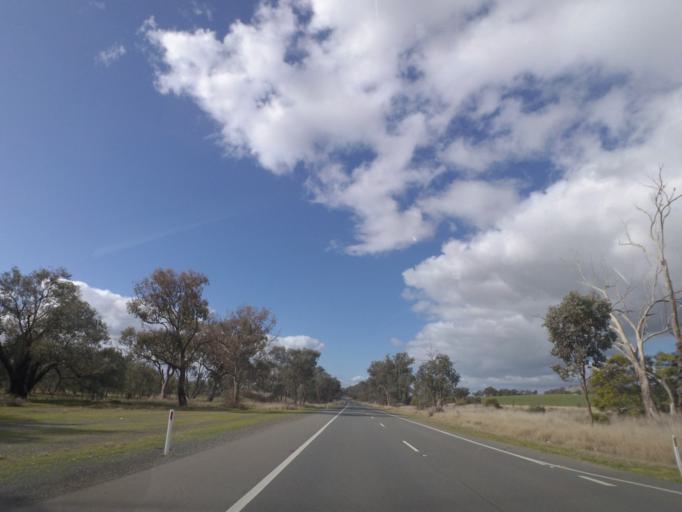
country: AU
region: New South Wales
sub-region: Greater Hume Shire
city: Holbrook
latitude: -35.6778
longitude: 147.3700
